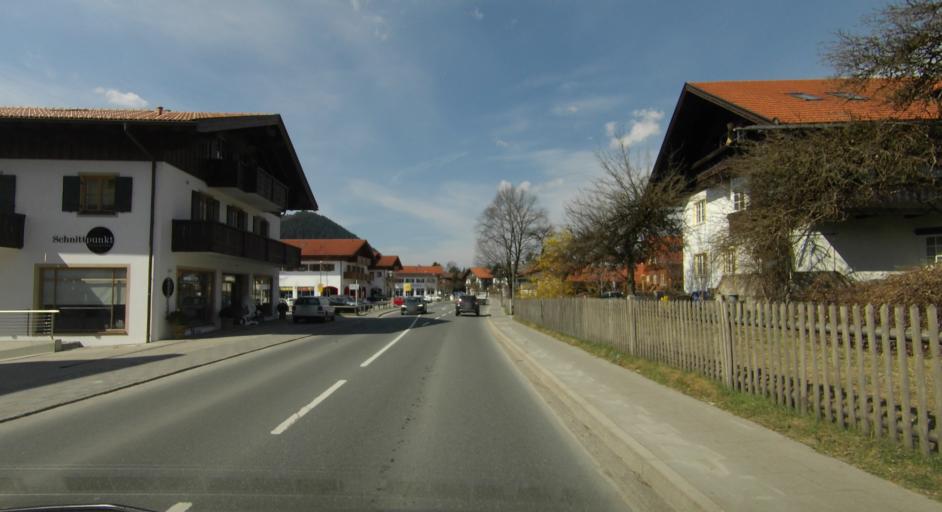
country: DE
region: Bavaria
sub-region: Upper Bavaria
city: Schliersee
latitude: 47.7372
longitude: 11.8588
